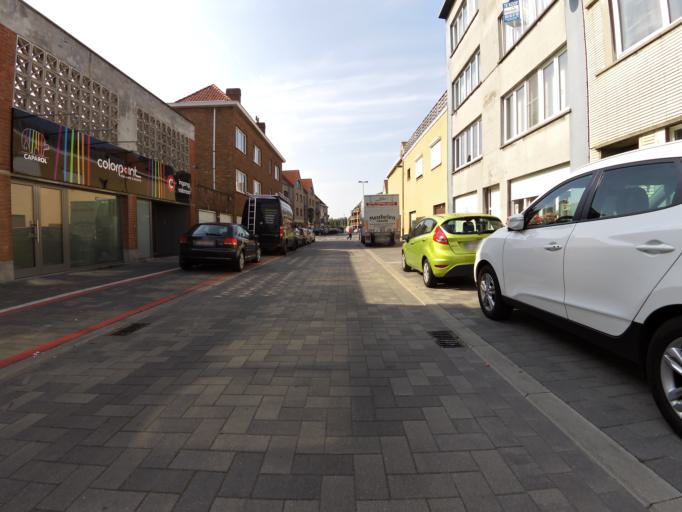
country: BE
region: Flanders
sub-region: Provincie West-Vlaanderen
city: Ostend
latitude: 51.2108
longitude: 2.9063
